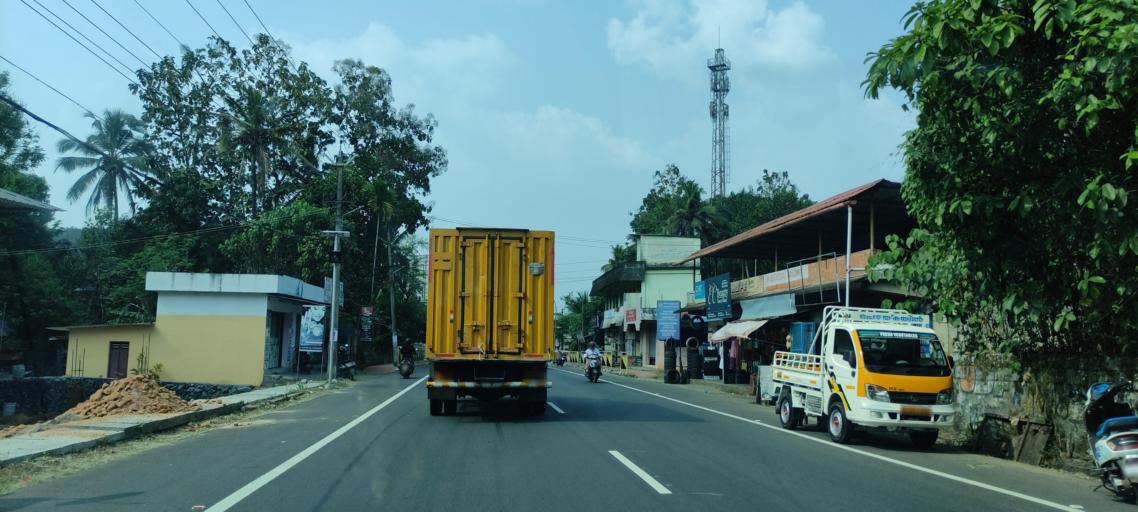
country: IN
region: Kerala
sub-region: Alappuzha
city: Chengannur
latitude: 9.2875
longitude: 76.6515
